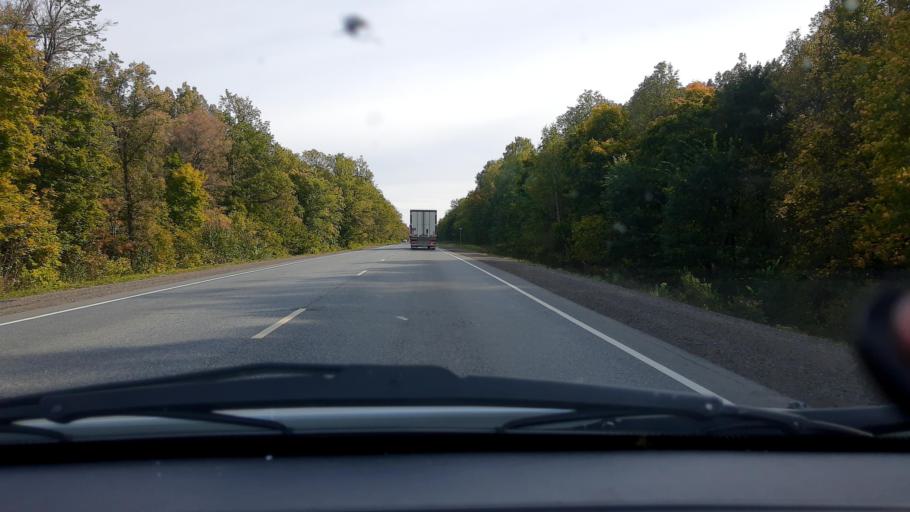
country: RU
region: Bashkortostan
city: Iglino
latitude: 54.7684
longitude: 56.4366
